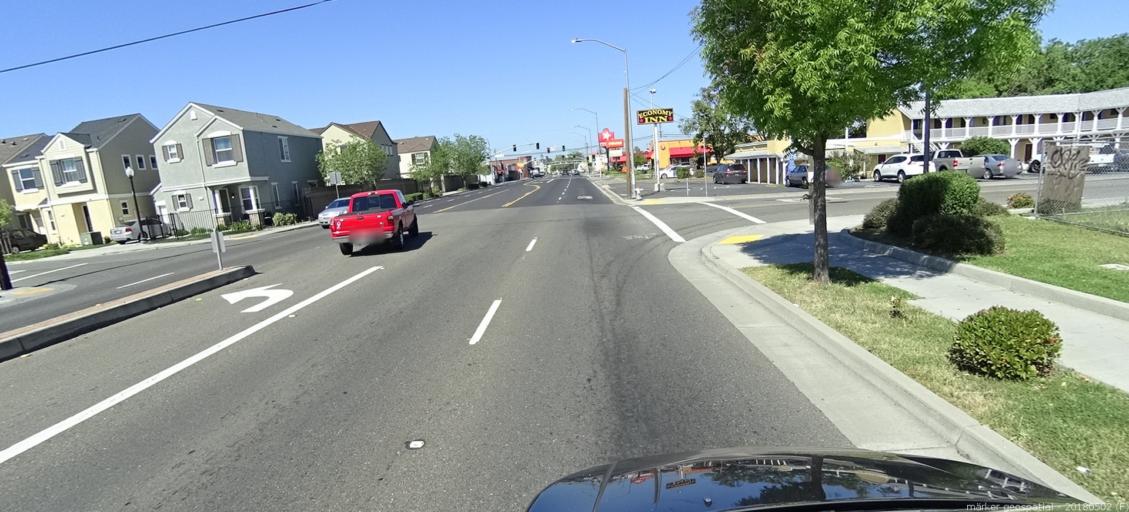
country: US
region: California
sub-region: Sacramento County
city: Sacramento
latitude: 38.6112
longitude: -121.4447
